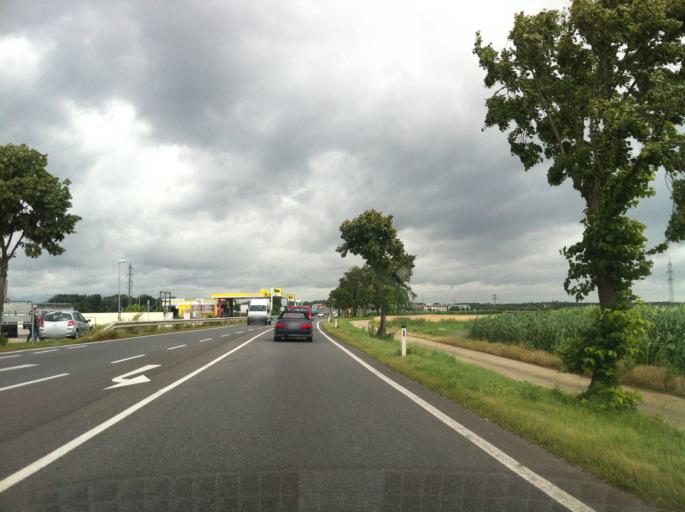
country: AT
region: Lower Austria
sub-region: Politischer Bezirk Tulln
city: Langenrohr
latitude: 48.3099
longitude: 16.0144
